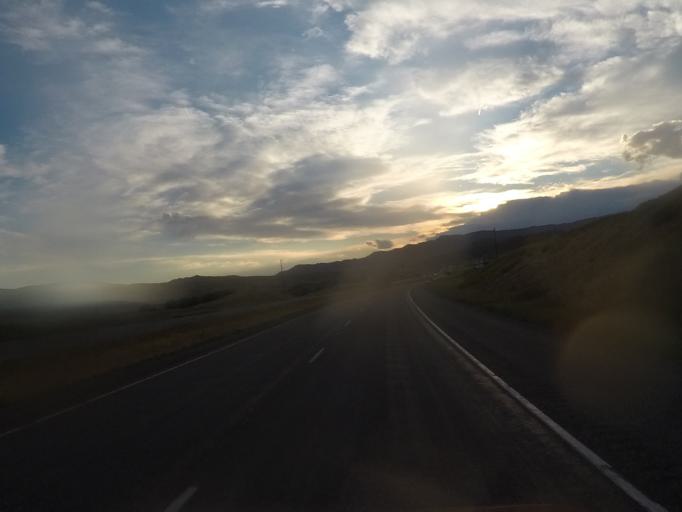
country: US
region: Montana
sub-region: Park County
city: Livingston
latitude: 45.6479
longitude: -110.6011
